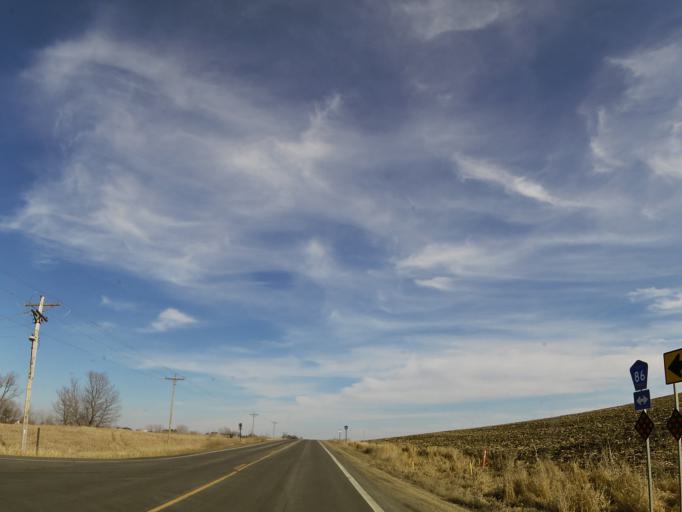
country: US
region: Minnesota
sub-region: Scott County
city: Elko New Market
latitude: 44.5440
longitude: -93.3399
